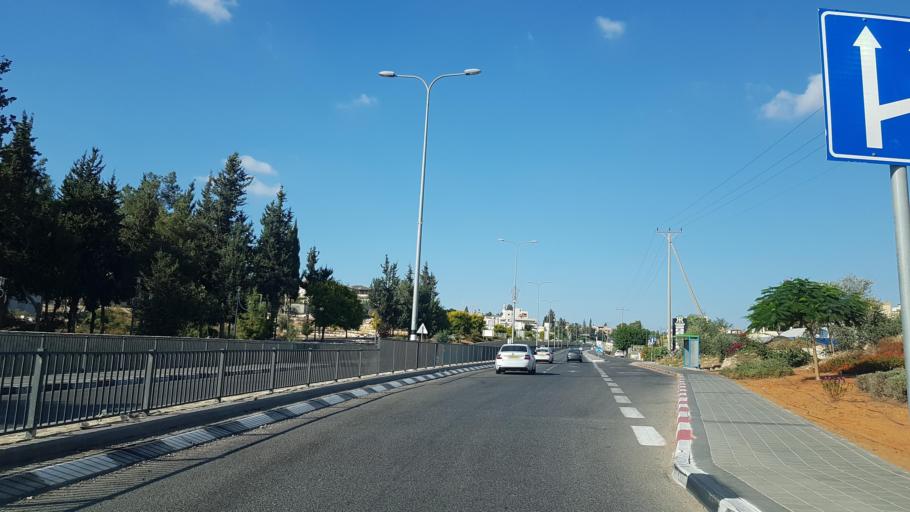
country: PS
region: West Bank
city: Zayta
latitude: 32.3618
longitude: 35.0301
